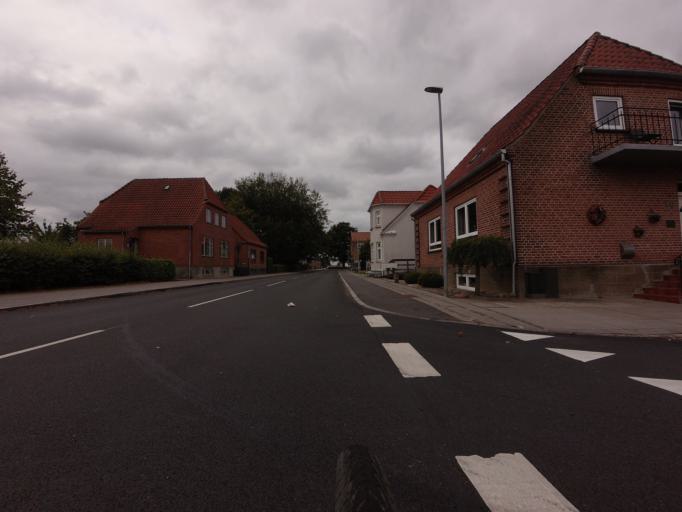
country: DK
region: South Denmark
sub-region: Billund Kommune
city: Grindsted
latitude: 55.7581
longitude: 8.9245
